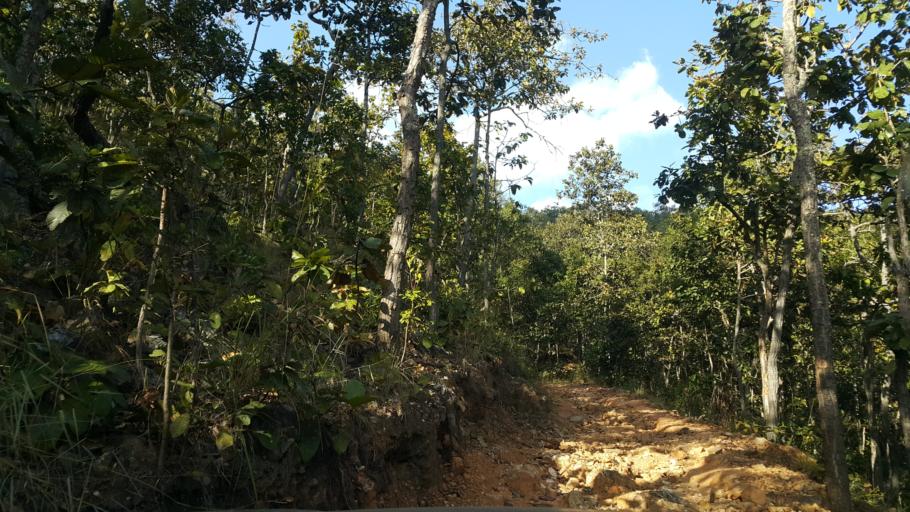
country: TH
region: Lamphun
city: Ban Thi
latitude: 18.6673
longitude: 99.2013
